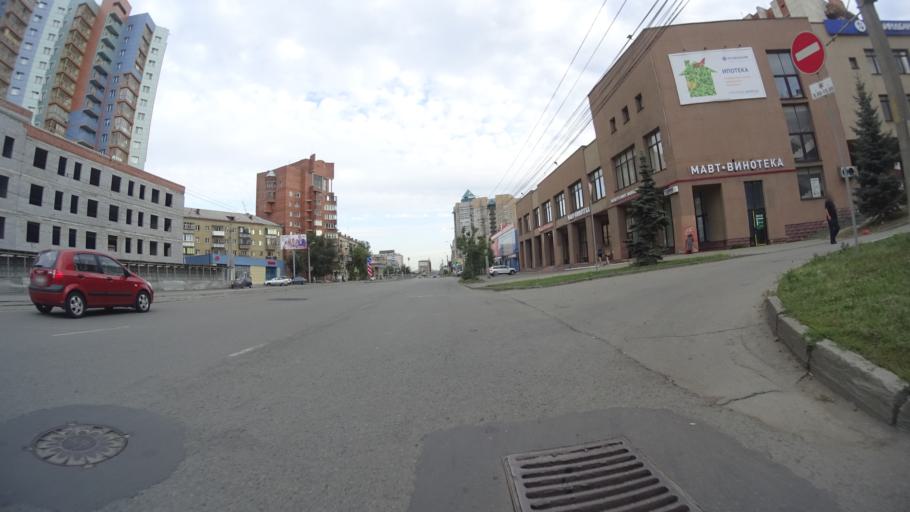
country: RU
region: Chelyabinsk
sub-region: Gorod Chelyabinsk
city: Chelyabinsk
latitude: 55.1474
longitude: 61.4122
